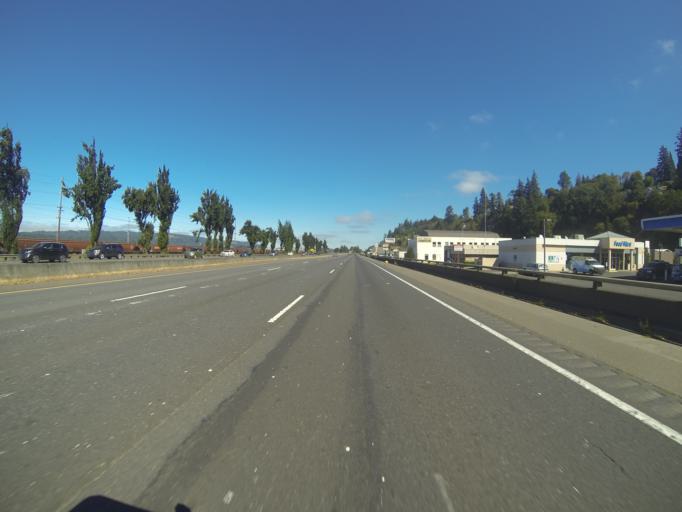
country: US
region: Washington
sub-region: Cowlitz County
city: Kalama
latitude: 46.0097
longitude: -122.8462
